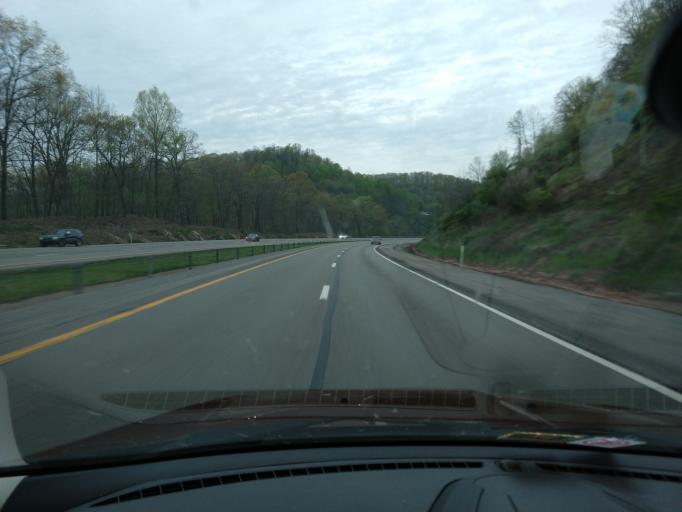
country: US
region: West Virginia
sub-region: Lewis County
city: Weston
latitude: 38.9911
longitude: -80.5058
